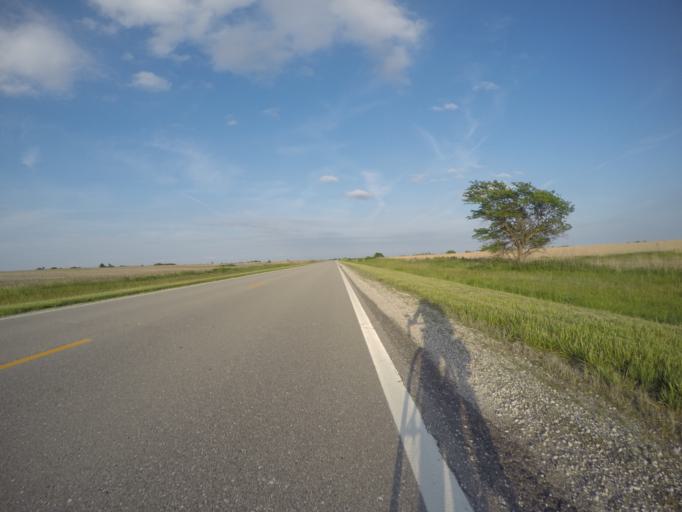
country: US
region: Kansas
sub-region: Pottawatomie County
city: Westmoreland
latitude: 39.4284
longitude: -96.5341
